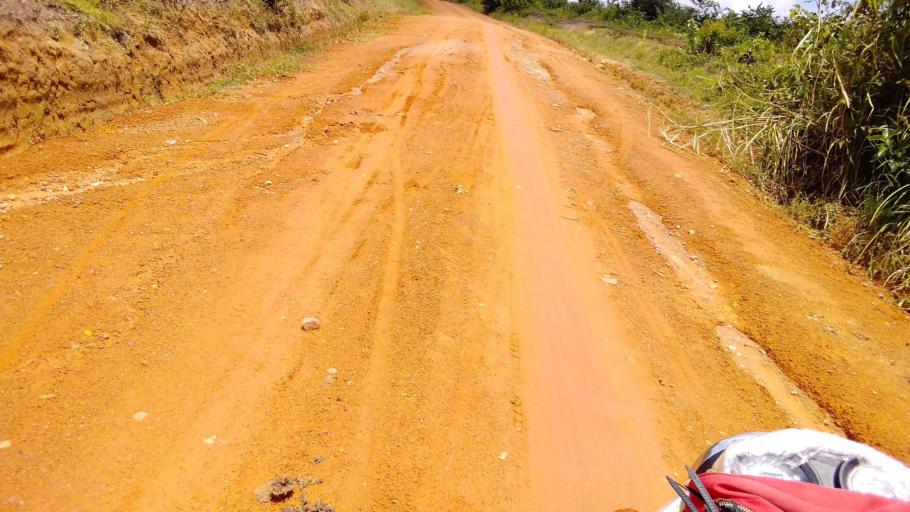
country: SL
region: Eastern Province
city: Koidu
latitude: 8.6921
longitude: -10.9247
